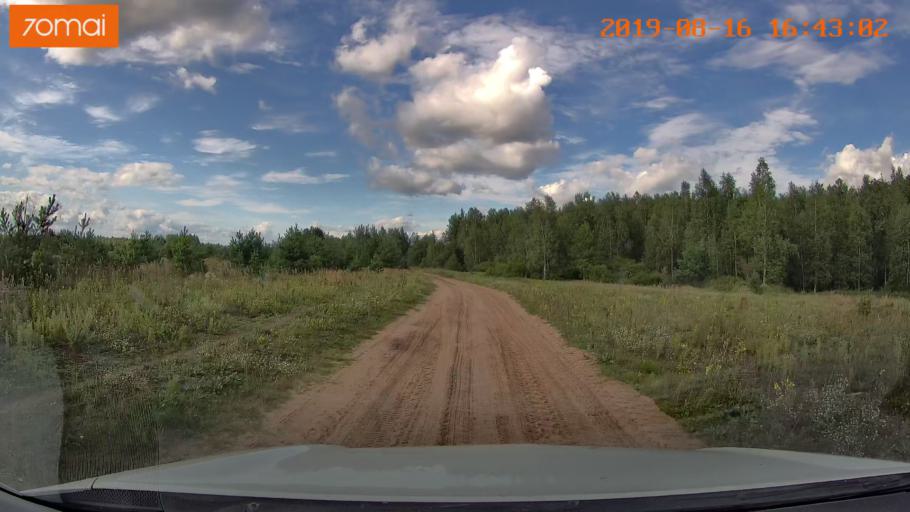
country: BY
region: Mogilev
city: Asipovichy
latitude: 53.2424
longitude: 28.7774
